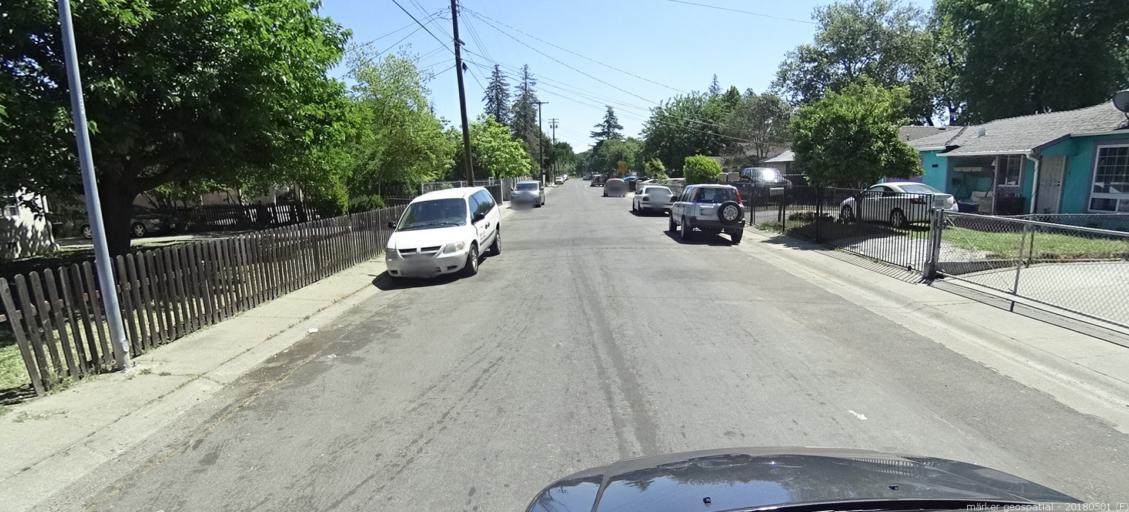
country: US
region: California
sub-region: Sacramento County
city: Rio Linda
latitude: 38.6288
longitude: -121.4379
